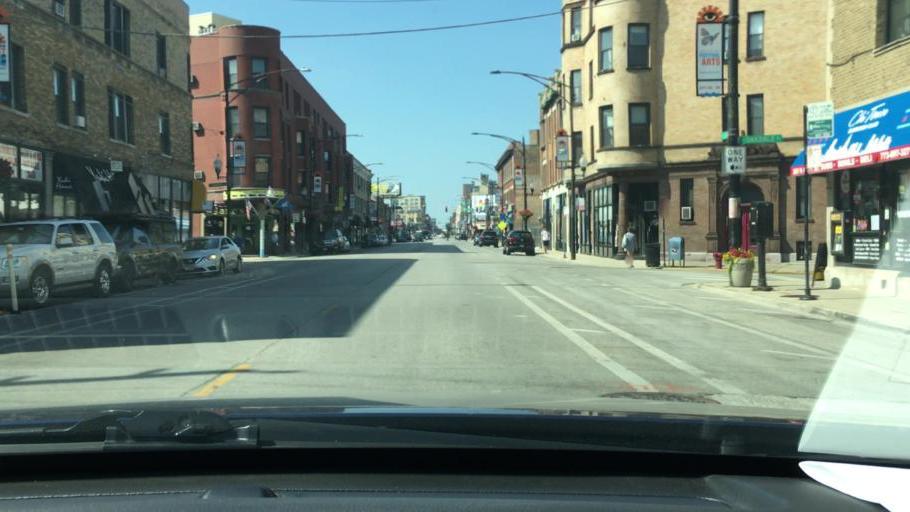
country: US
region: Illinois
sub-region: Cook County
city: Chicago
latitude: 41.9353
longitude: -87.6469
